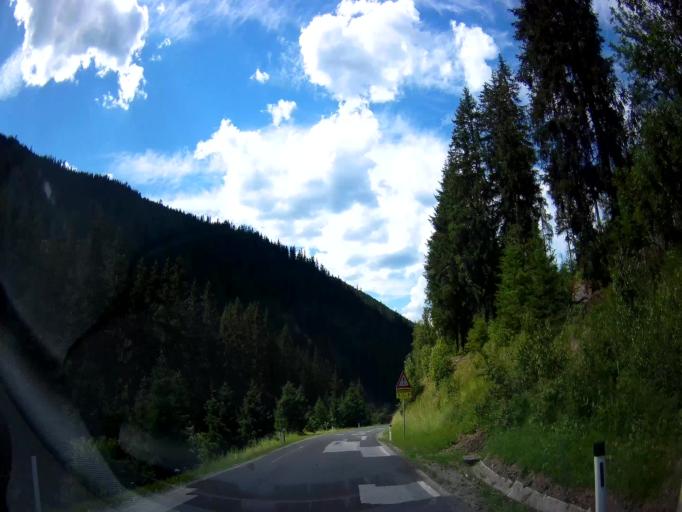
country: AT
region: Styria
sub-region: Politischer Bezirk Murau
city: Stadl an der Mur
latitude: 47.0311
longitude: 14.0072
